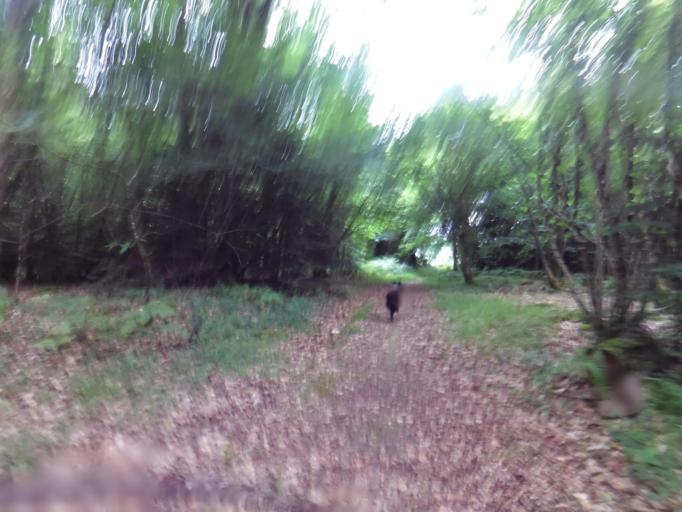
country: FR
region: Brittany
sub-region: Departement du Morbihan
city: Molac
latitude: 47.7629
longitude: -2.4299
